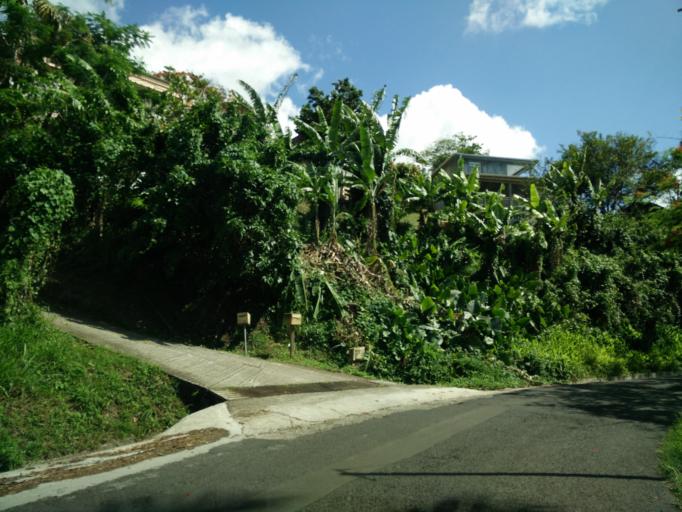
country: MQ
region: Martinique
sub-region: Martinique
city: Les Trois-Ilets
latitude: 14.5185
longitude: -61.0742
